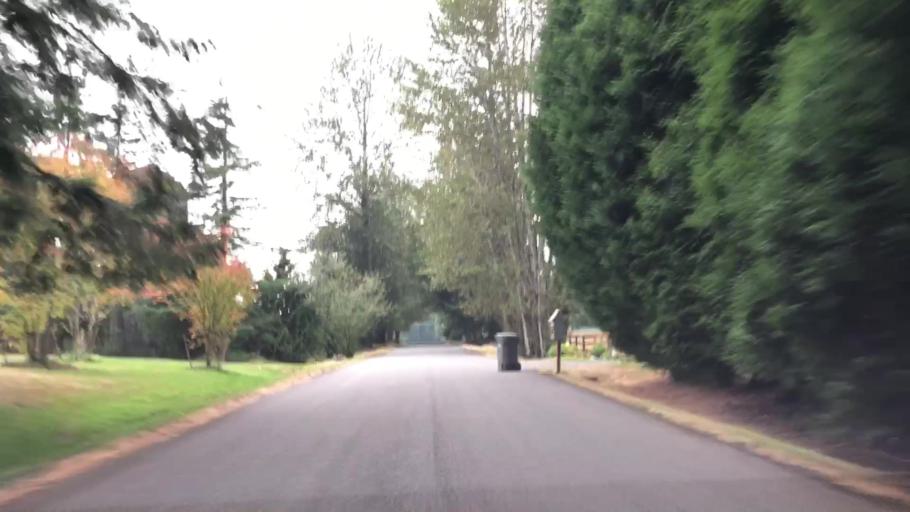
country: US
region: Washington
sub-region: King County
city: Cottage Lake
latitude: 47.7381
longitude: -122.1116
